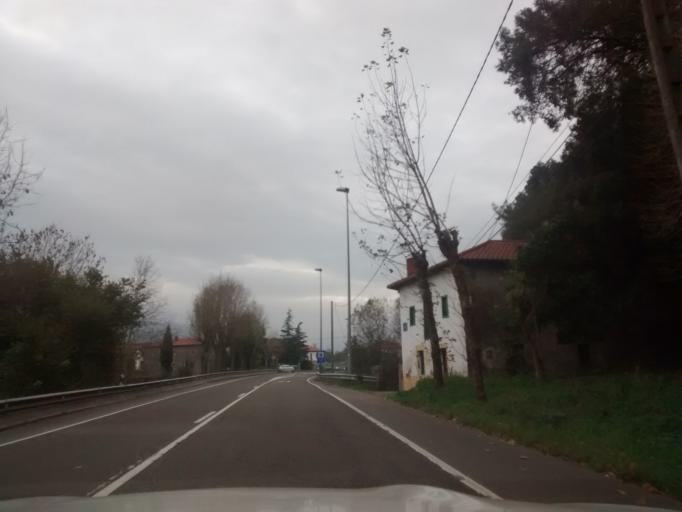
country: ES
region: Cantabria
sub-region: Provincia de Cantabria
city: Corvera
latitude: 43.2781
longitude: -3.9473
